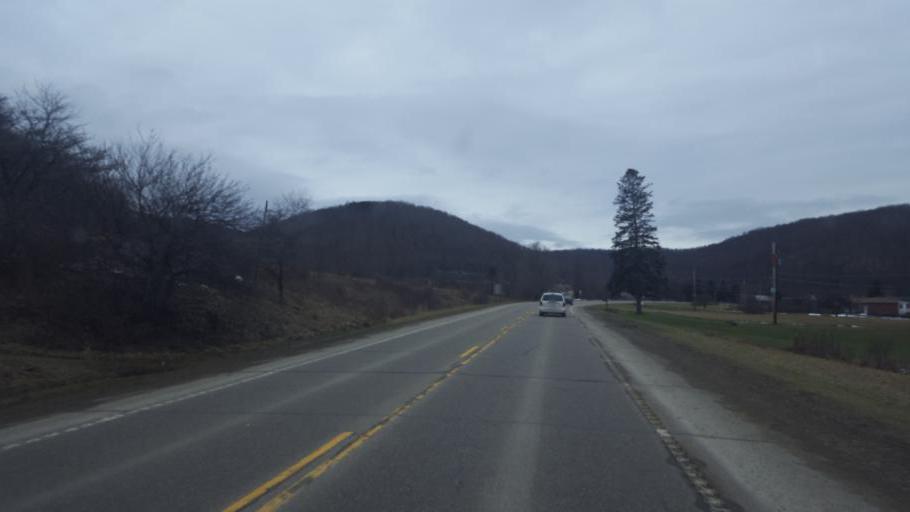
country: US
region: Pennsylvania
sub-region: Potter County
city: Coudersport
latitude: 41.8064
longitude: -78.0174
